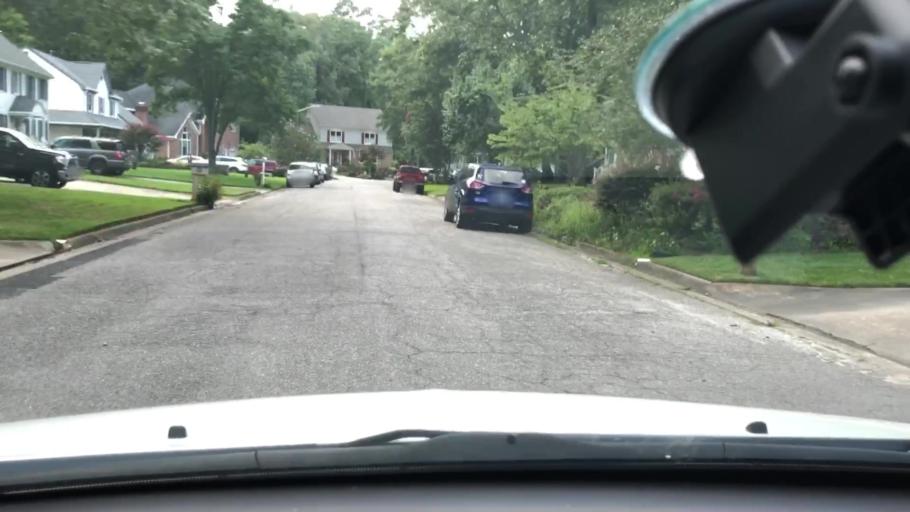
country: US
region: Virginia
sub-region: City of Chesapeake
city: Chesapeake
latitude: 36.7026
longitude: -76.2904
